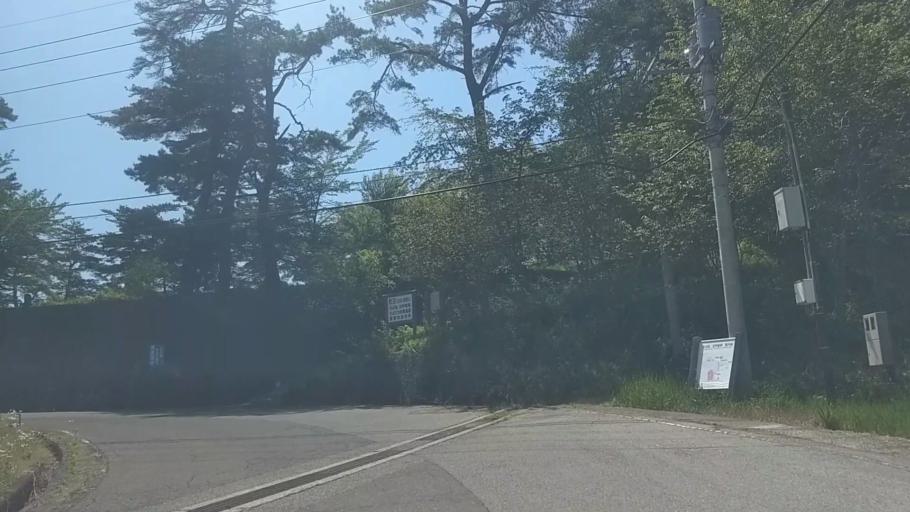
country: JP
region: Yamanashi
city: Nirasaki
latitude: 35.8904
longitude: 138.4551
